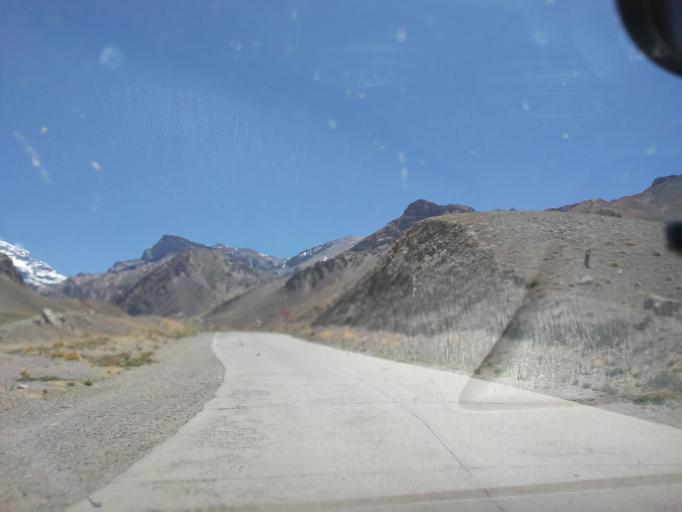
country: CL
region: Valparaiso
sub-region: Provincia de Los Andes
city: Los Andes
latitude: -32.8231
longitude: -69.9422
